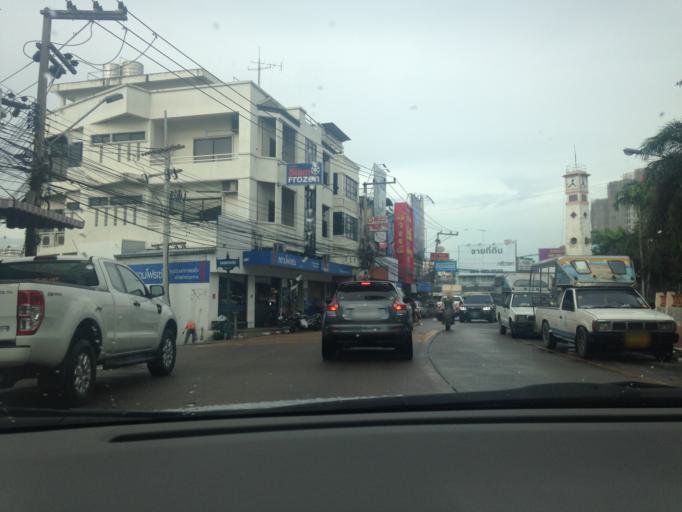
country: TH
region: Chon Buri
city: Si Racha
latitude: 13.1640
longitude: 100.9214
